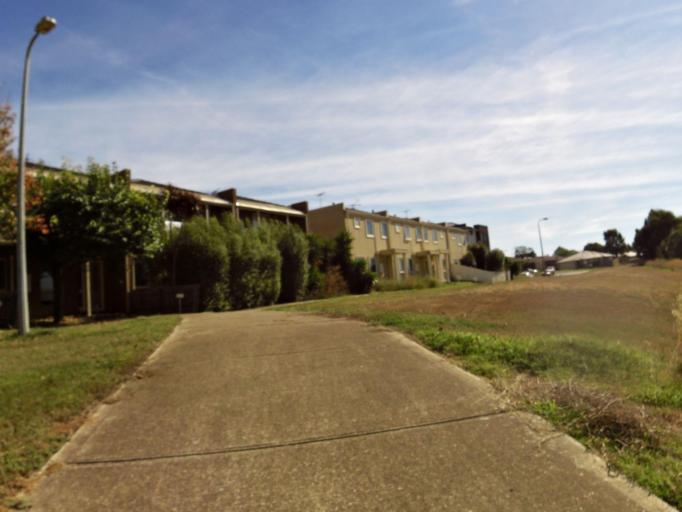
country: AU
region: Victoria
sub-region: Melton
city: Melton West
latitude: -37.6628
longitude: 144.5656
